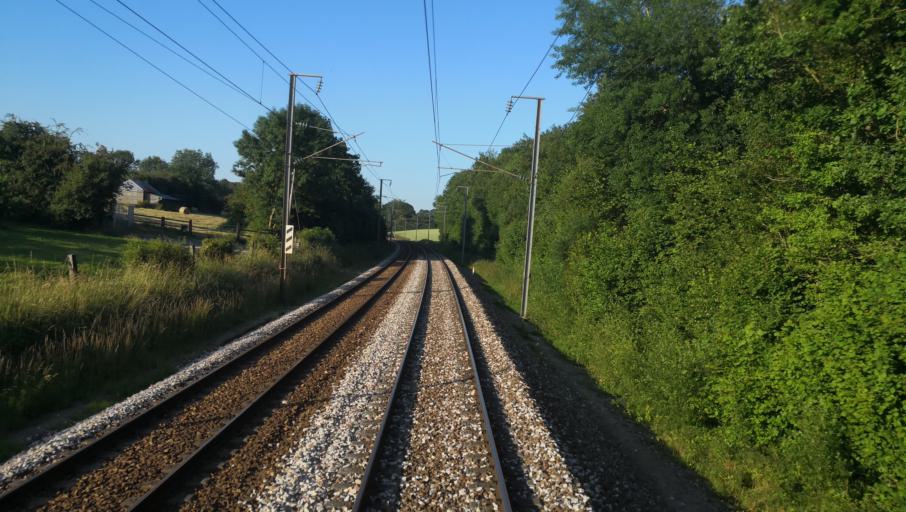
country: FR
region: Haute-Normandie
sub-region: Departement de l'Eure
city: Broglie
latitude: 49.0839
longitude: 0.5151
